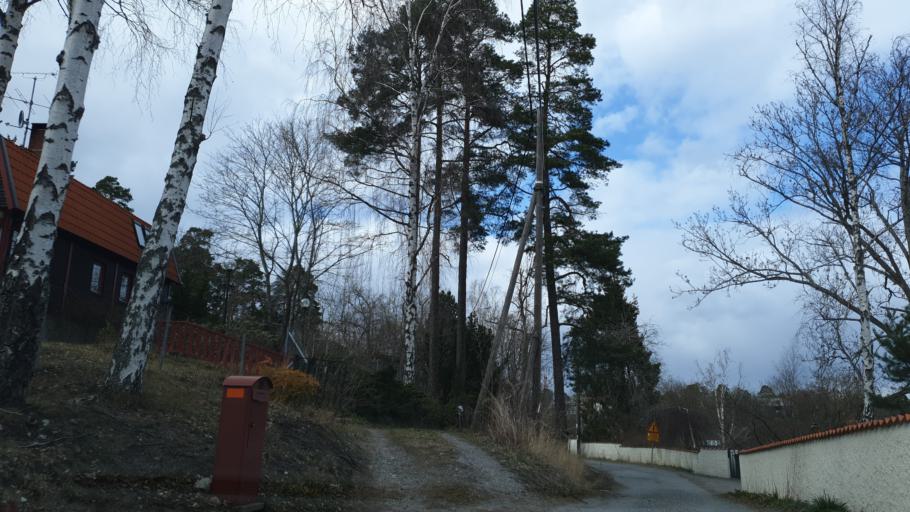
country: SE
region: Stockholm
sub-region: Nacka Kommun
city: Boo
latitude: 59.3235
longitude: 18.3119
